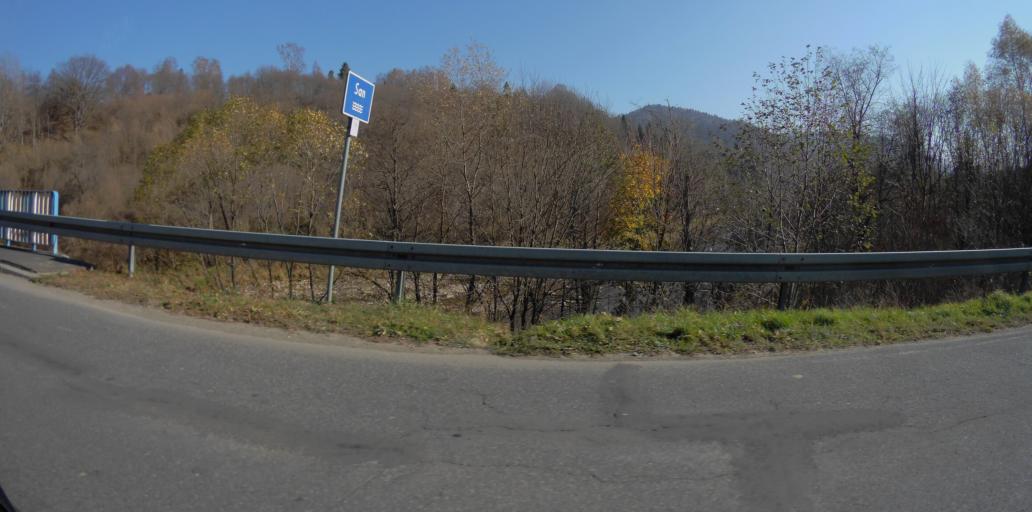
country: PL
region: Subcarpathian Voivodeship
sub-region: Powiat bieszczadzki
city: Lutowiska
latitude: 49.1999
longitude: 22.6750
